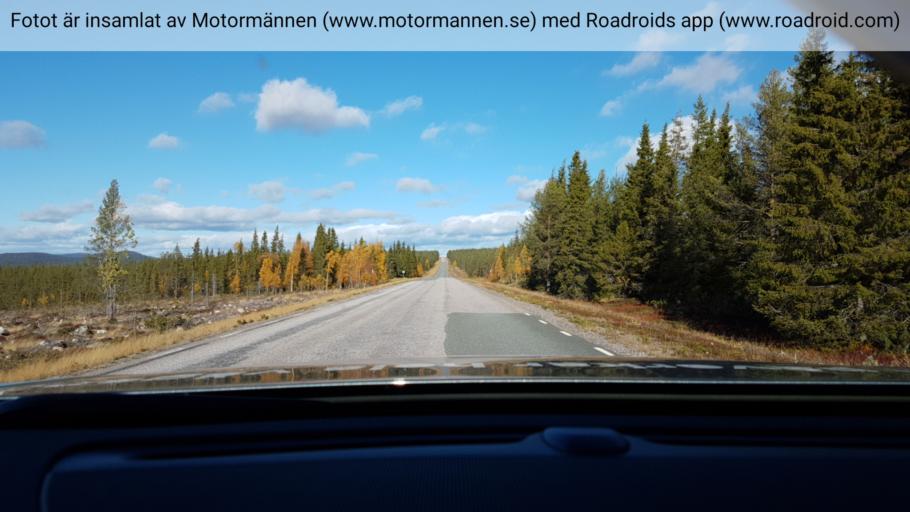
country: SE
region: Norrbotten
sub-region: Arjeplogs Kommun
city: Arjeplog
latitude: 65.8194
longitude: 18.4417
